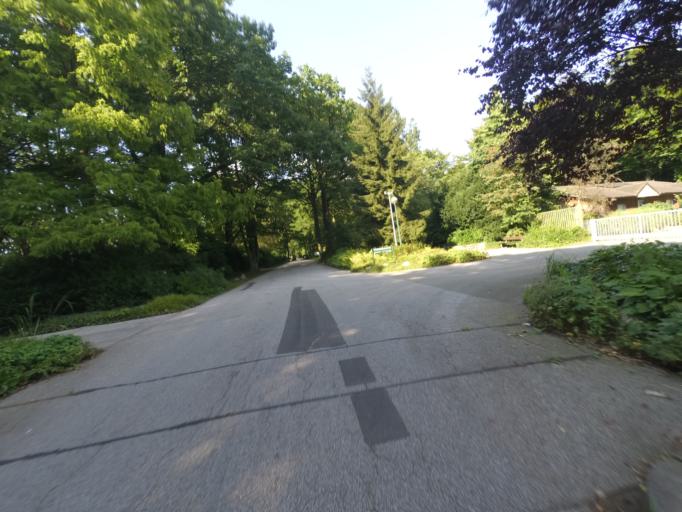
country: DE
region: Hamburg
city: Wandsbek
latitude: 53.5516
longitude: 10.1276
